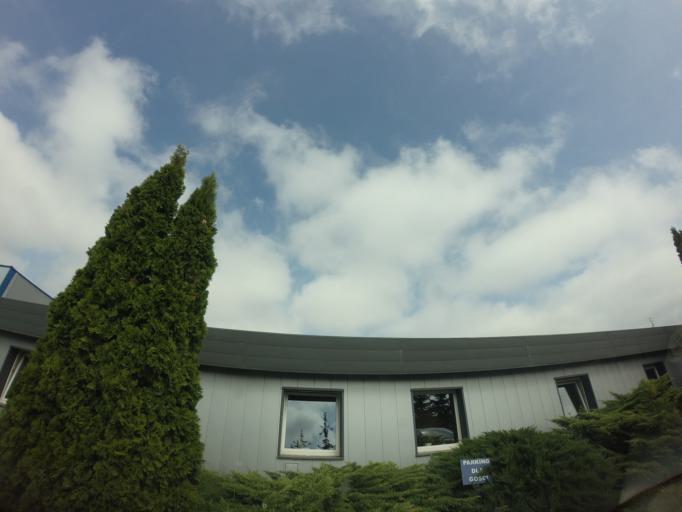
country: PL
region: Greater Poland Voivodeship
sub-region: Powiat miedzychodzki
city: Miedzychod
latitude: 52.6107
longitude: 15.9073
